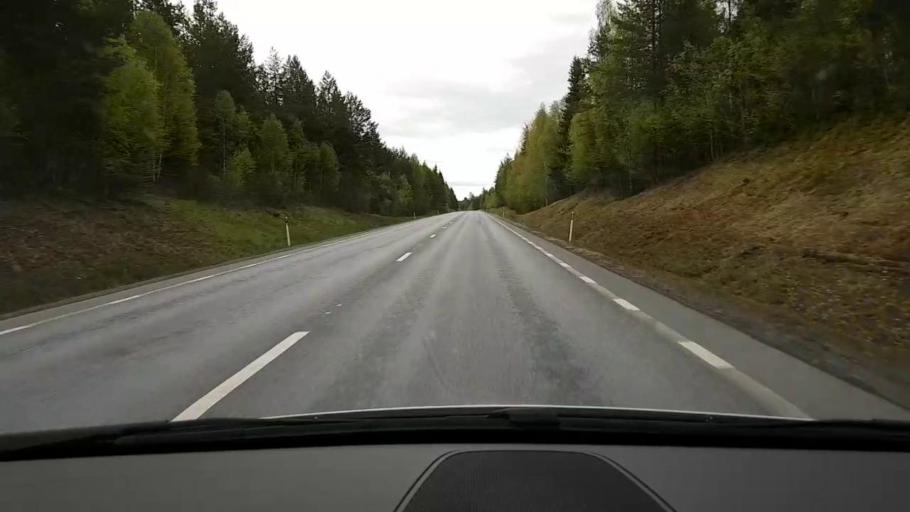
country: SE
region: Jaemtland
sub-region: Krokoms Kommun
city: Krokom
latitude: 63.3213
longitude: 14.2395
